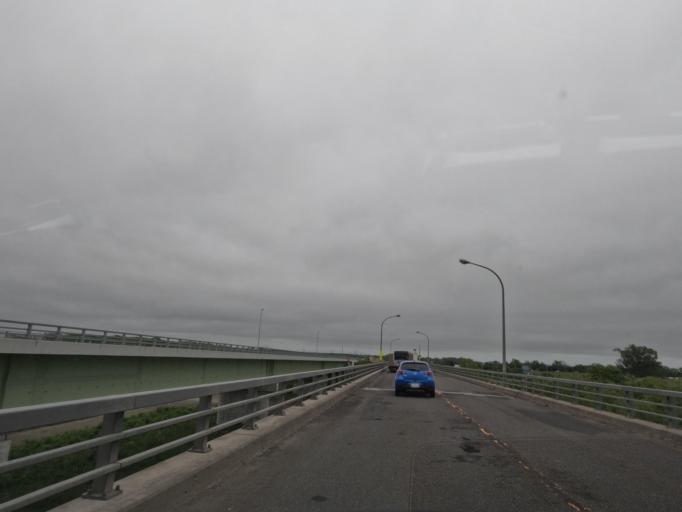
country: JP
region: Hokkaido
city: Ebetsu
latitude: 43.1371
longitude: 141.5128
